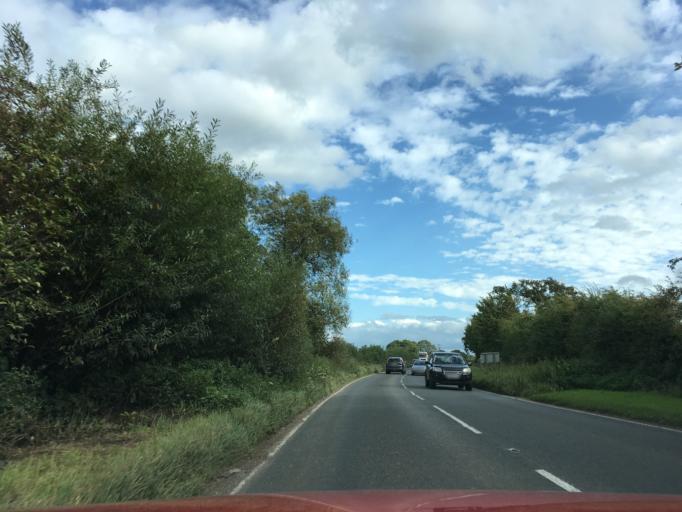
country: GB
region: England
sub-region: South Gloucestershire
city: Charfield
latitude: 51.6296
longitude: -2.4221
